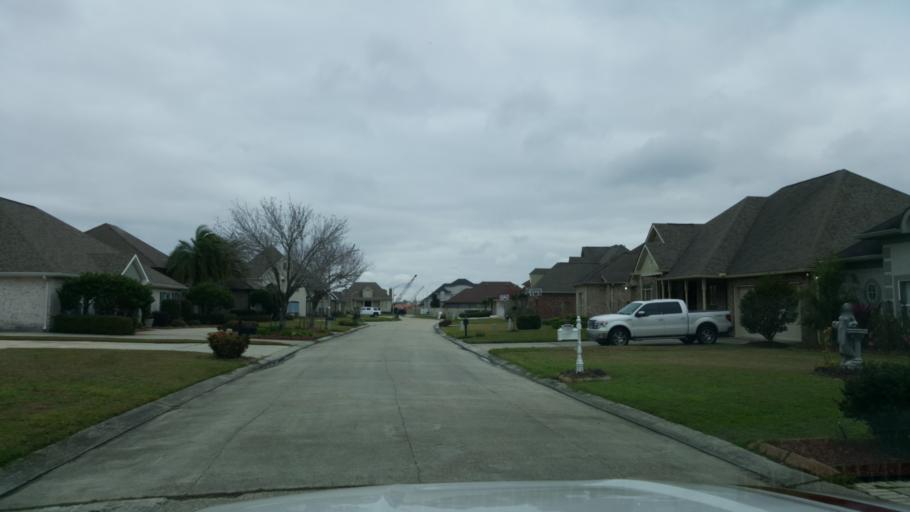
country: US
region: Louisiana
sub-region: Jefferson Parish
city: Woodmere
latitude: 29.8784
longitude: -90.0795
